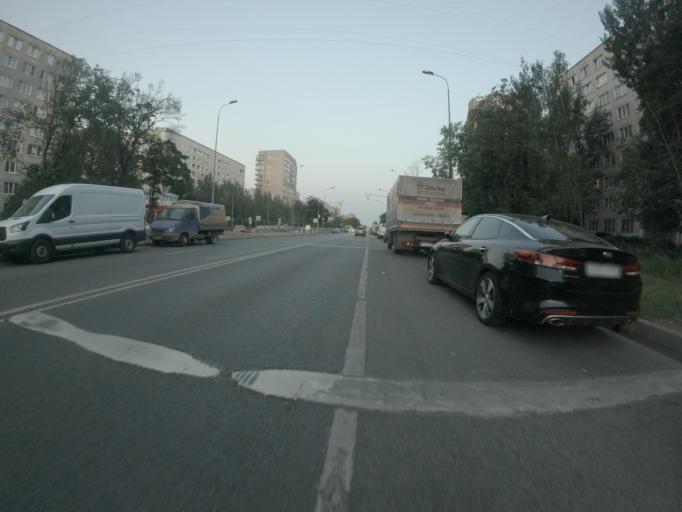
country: RU
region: St.-Petersburg
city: Krasnogvargeisky
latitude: 59.9191
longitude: 30.4813
